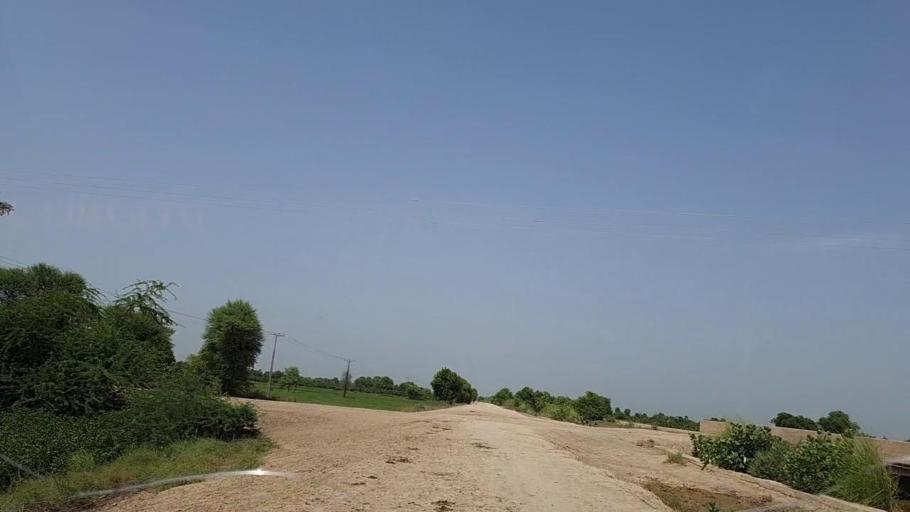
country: PK
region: Sindh
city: Kandiaro
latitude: 27.0340
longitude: 68.1485
